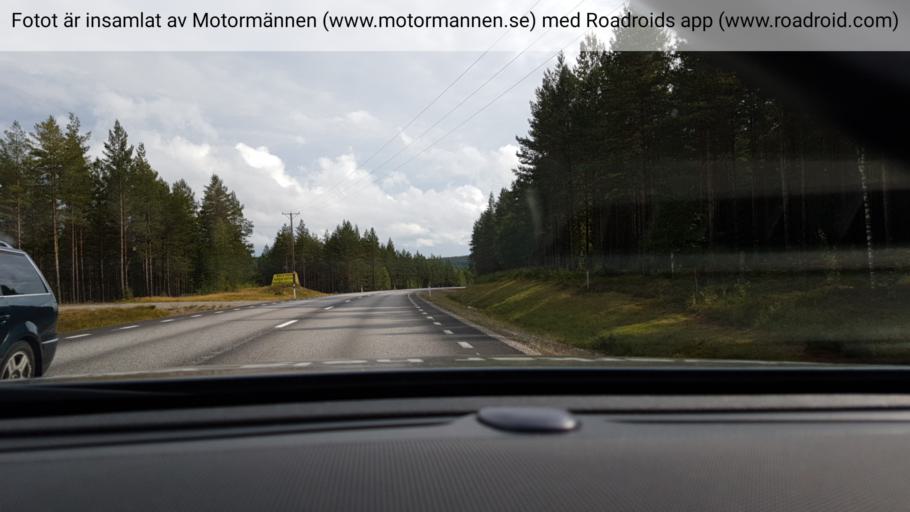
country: SE
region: Dalarna
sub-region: Rattviks Kommun
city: Raettvik
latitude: 60.8223
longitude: 15.2545
